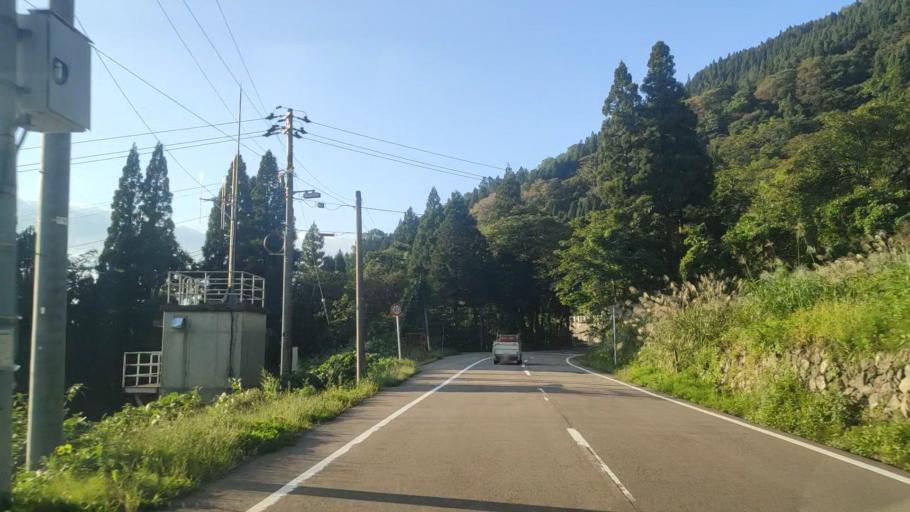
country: JP
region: Toyama
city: Yatsuomachi-higashikumisaka
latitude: 36.4975
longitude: 137.0261
